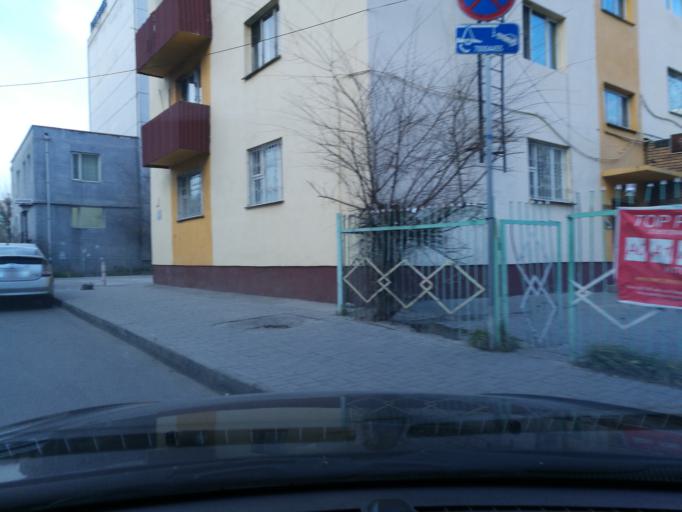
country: MN
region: Ulaanbaatar
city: Ulaanbaatar
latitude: 47.9220
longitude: 106.9257
